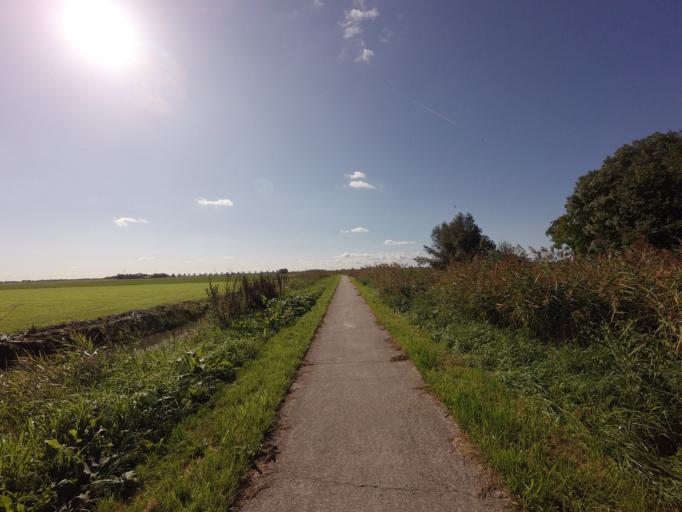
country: NL
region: Friesland
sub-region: Gemeente Boarnsterhim
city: Reduzum
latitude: 53.1286
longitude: 5.7556
